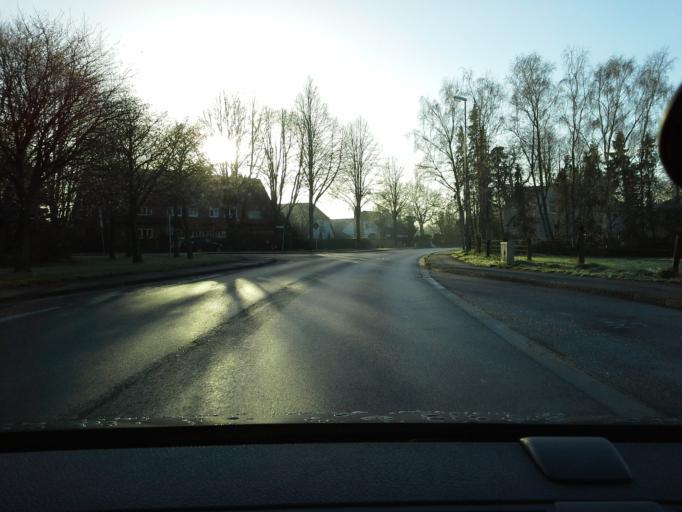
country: DE
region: Schleswig-Holstein
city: Quickborn
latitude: 53.7283
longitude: 9.8903
